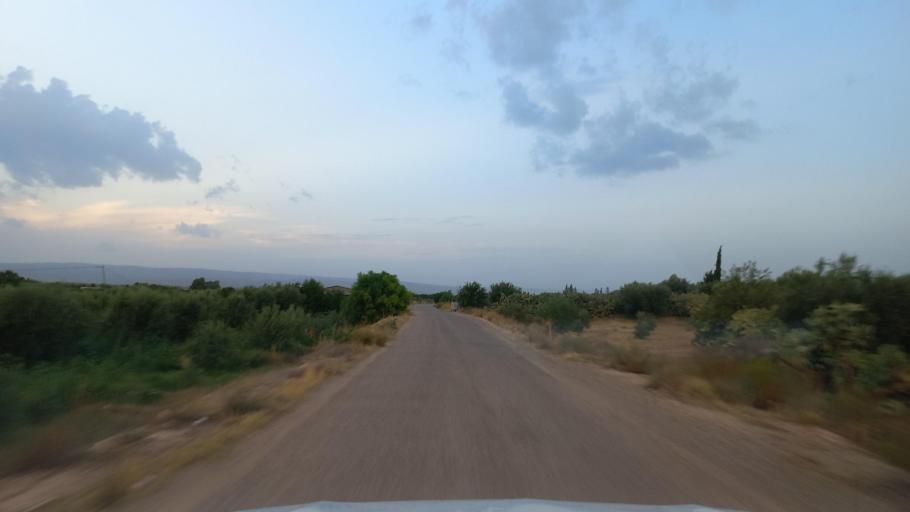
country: TN
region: Al Qasrayn
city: Kasserine
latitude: 35.2688
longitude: 9.0480
